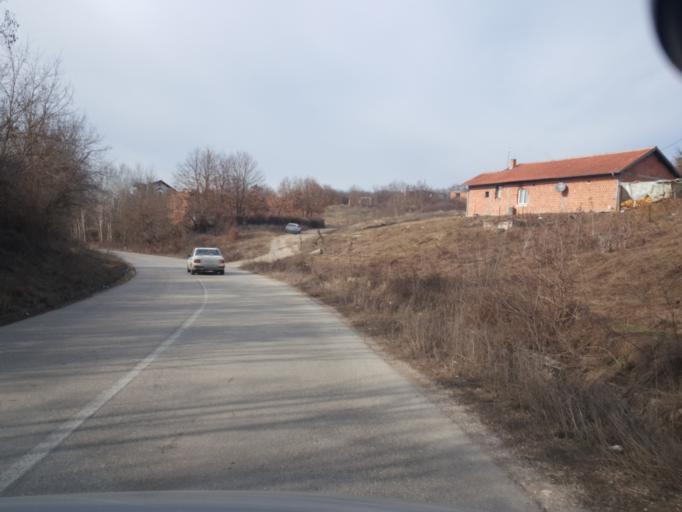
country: XK
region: Pec
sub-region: Komuna e Klines
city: Klina
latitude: 42.6750
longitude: 20.5290
